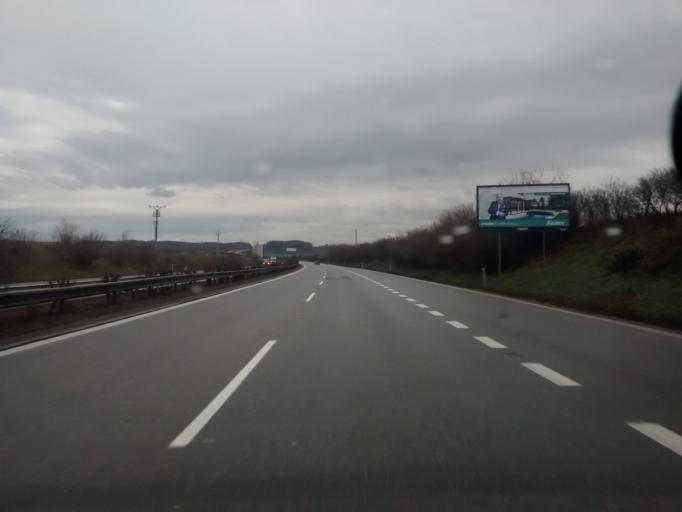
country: CZ
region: Central Bohemia
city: Odolena Voda
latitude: 50.2439
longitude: 14.3779
